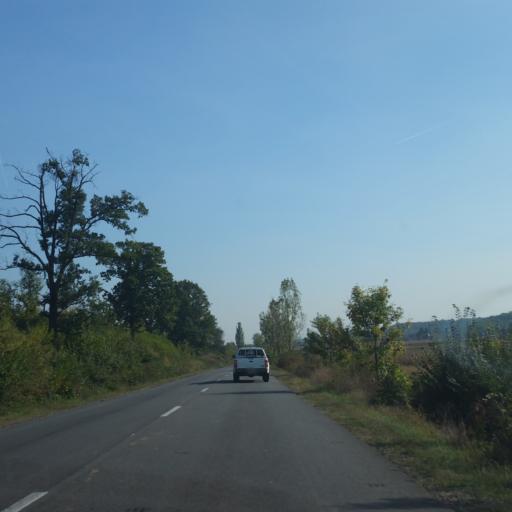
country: RO
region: Arges
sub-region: Comuna Merisani
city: Merisani
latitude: 44.9582
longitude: 24.7558
